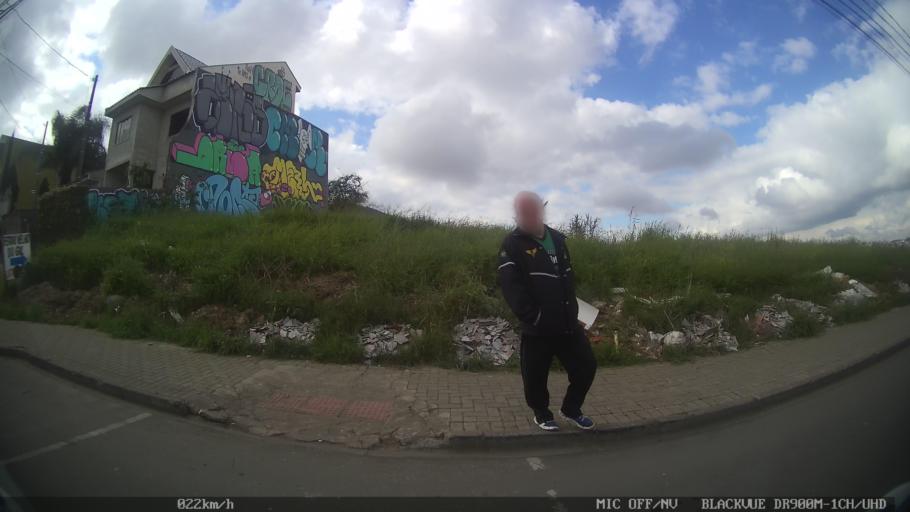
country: BR
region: Parana
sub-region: Pinhais
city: Pinhais
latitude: -25.3667
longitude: -49.2010
